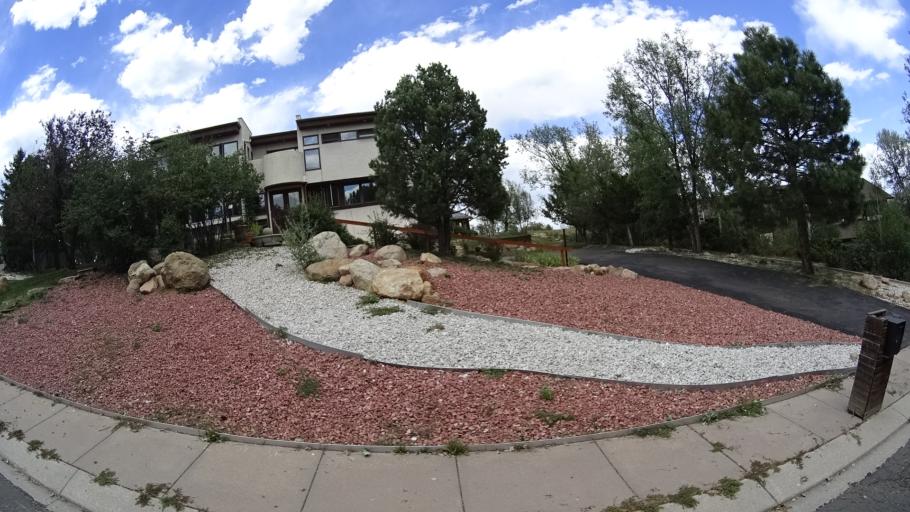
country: US
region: Colorado
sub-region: El Paso County
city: Stratmoor
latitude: 38.7723
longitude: -104.8332
